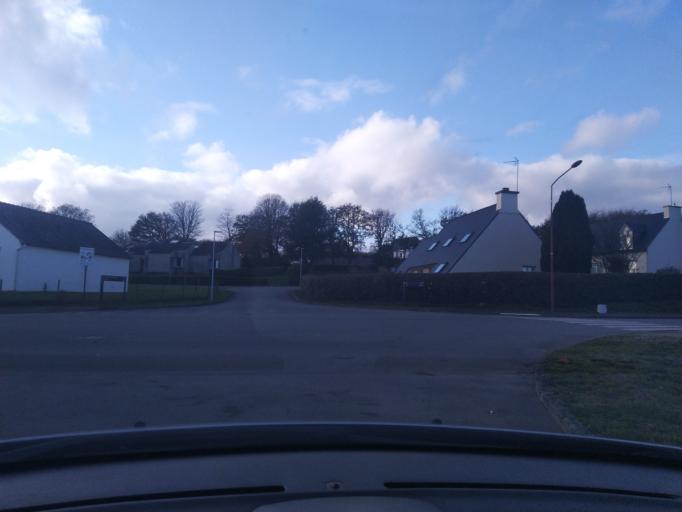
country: FR
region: Brittany
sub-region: Departement du Finistere
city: Guerlesquin
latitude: 48.5141
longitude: -3.5874
